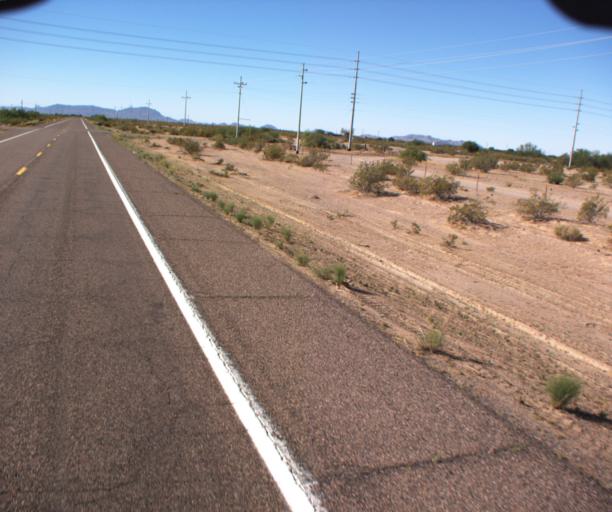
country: US
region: Arizona
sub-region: Maricopa County
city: Gila Bend
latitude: 32.9284
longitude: -112.7341
